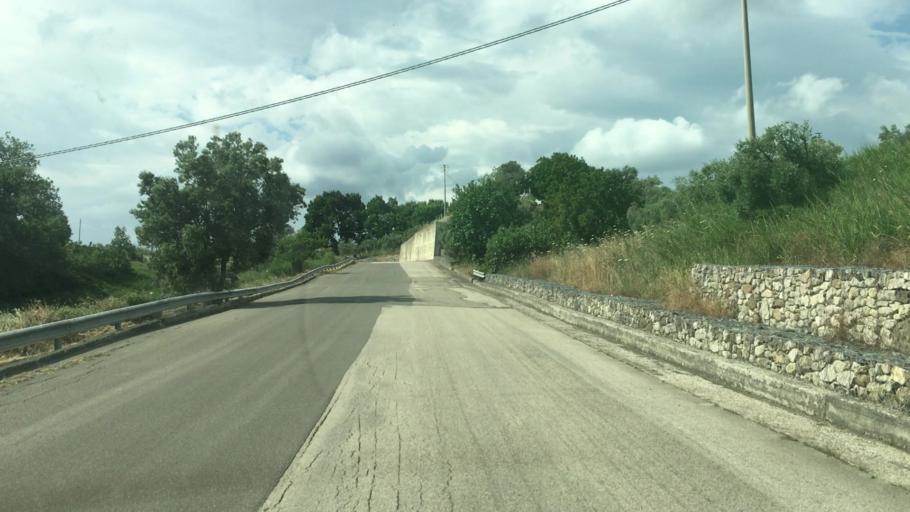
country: IT
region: Basilicate
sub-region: Provincia di Matera
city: San Mauro Forte
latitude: 40.4810
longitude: 16.2668
